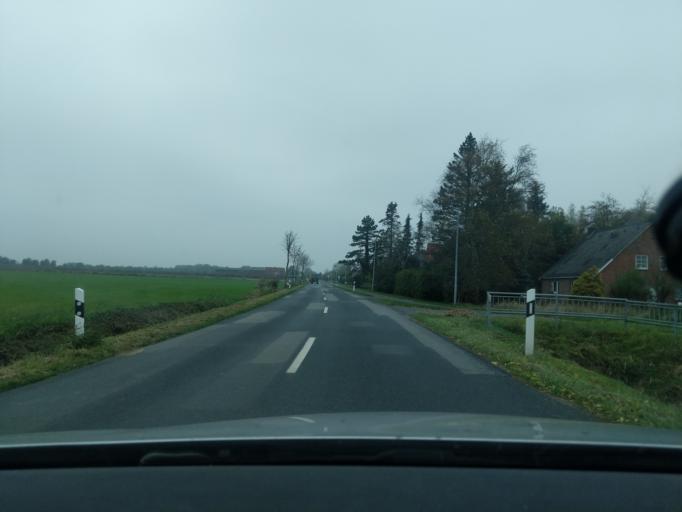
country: DE
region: Lower Saxony
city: Otterndorf
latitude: 53.8204
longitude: 8.8606
